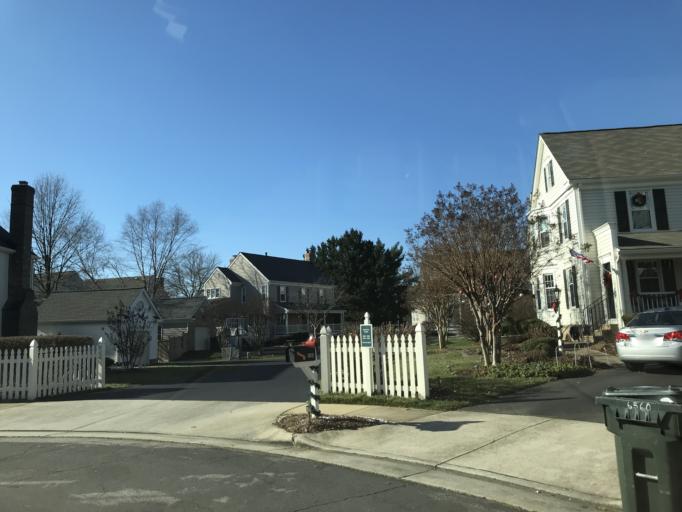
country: US
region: Virginia
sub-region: Fairfax County
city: Franconia
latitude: 38.7776
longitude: -77.1670
